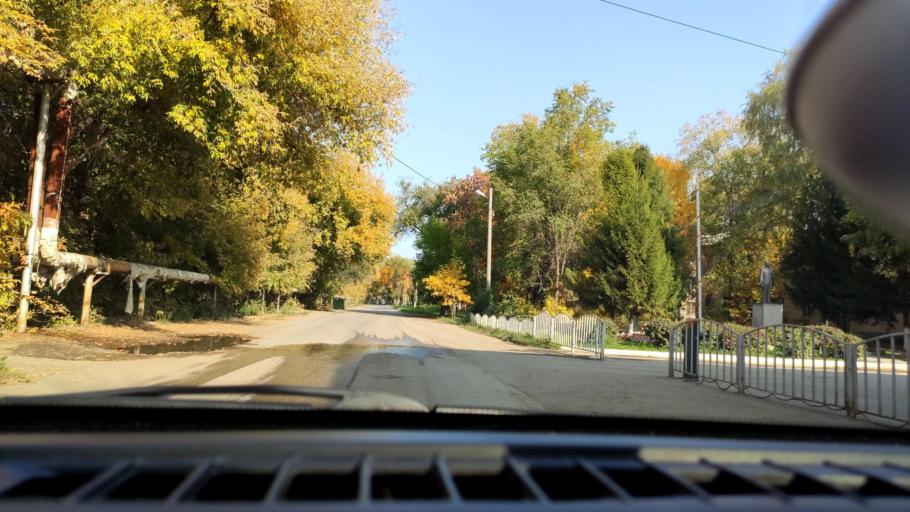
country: RU
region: Samara
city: Smyshlyayevka
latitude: 53.1888
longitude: 50.2876
